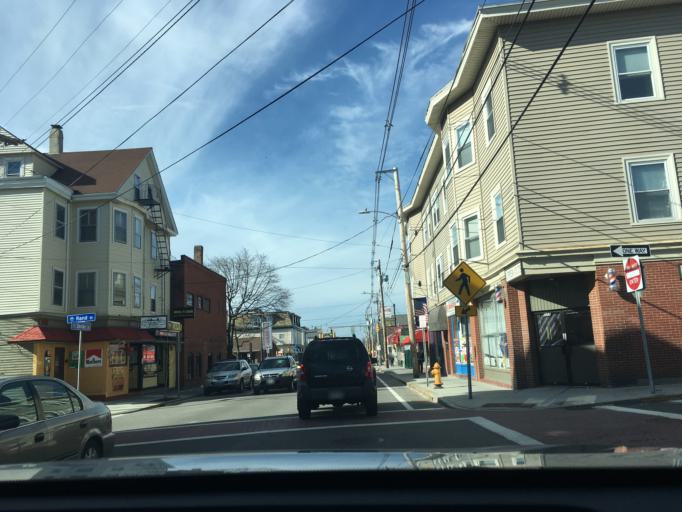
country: US
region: Rhode Island
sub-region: Providence County
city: Central Falls
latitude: 41.8846
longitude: -71.3946
